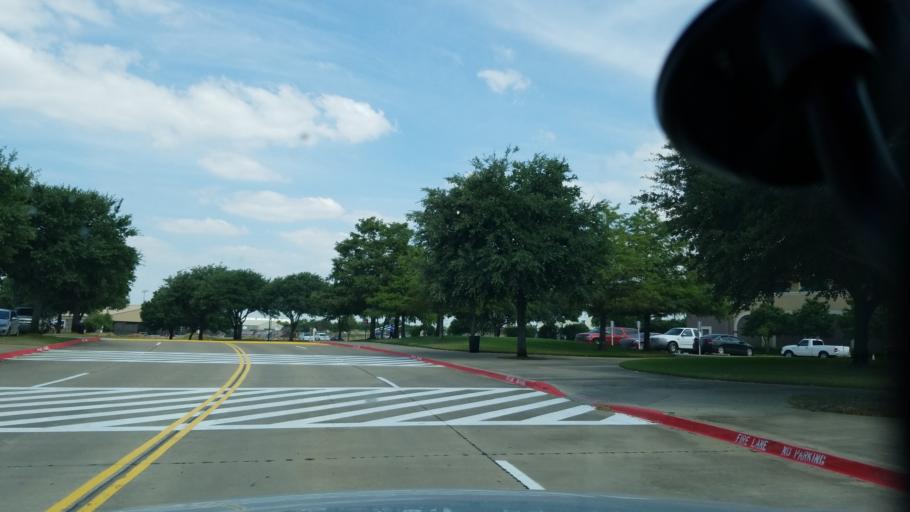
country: US
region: Texas
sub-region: Dallas County
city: Grand Prairie
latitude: 32.7724
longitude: -96.9905
